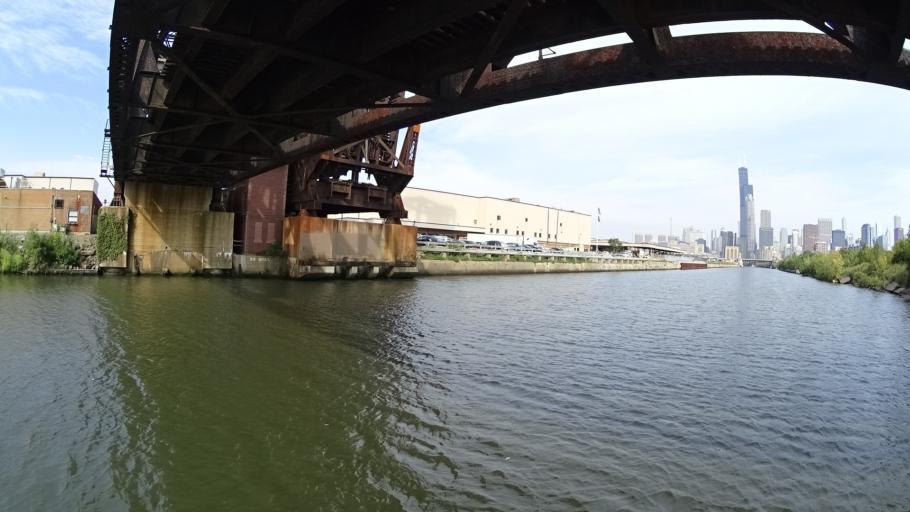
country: US
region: Illinois
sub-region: Cook County
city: Chicago
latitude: 41.8609
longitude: -87.6345
